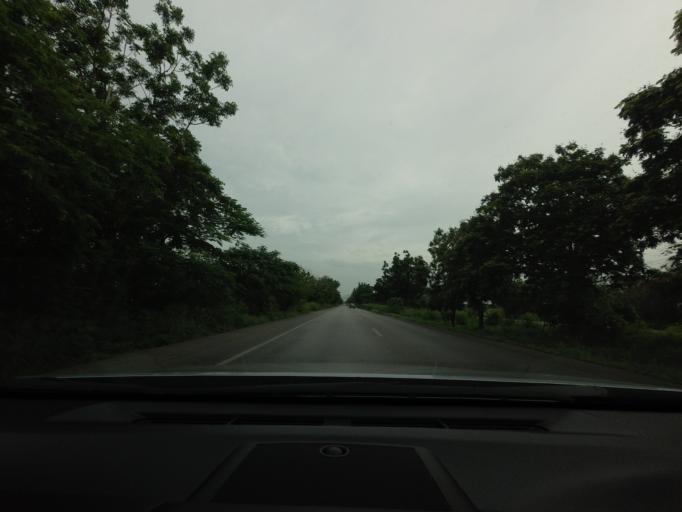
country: TH
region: Phetchaburi
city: Cha-am
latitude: 12.7438
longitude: 99.9301
